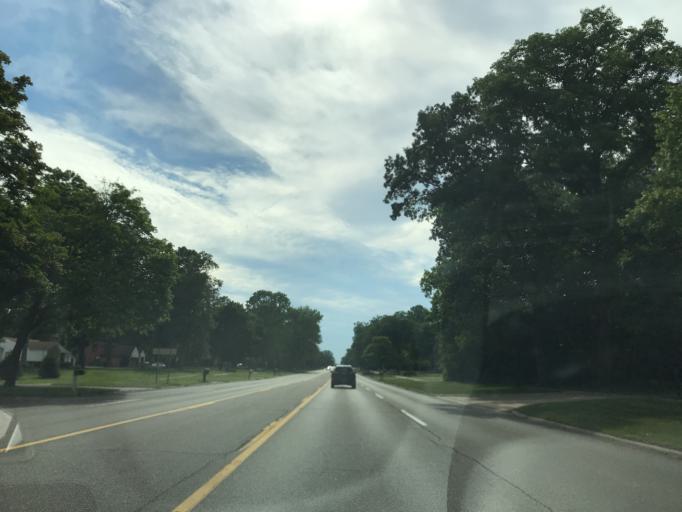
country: US
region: Michigan
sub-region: Wayne County
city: Livonia
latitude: 42.4122
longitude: -83.3558
